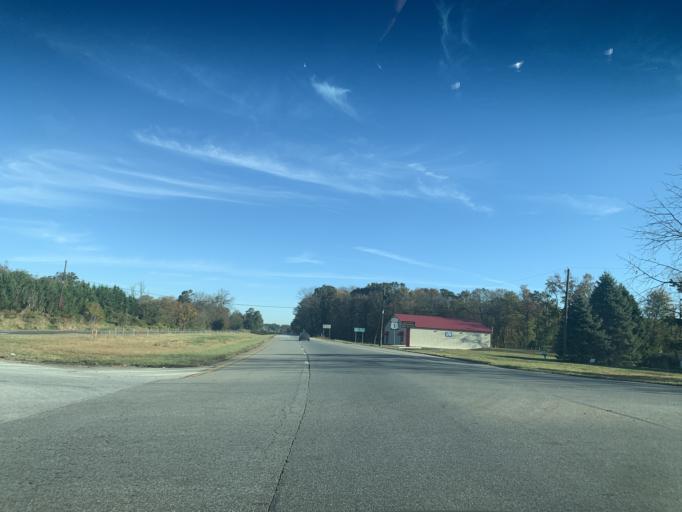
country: US
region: Maryland
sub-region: Cecil County
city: Rising Sun
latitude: 39.7242
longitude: -76.0285
